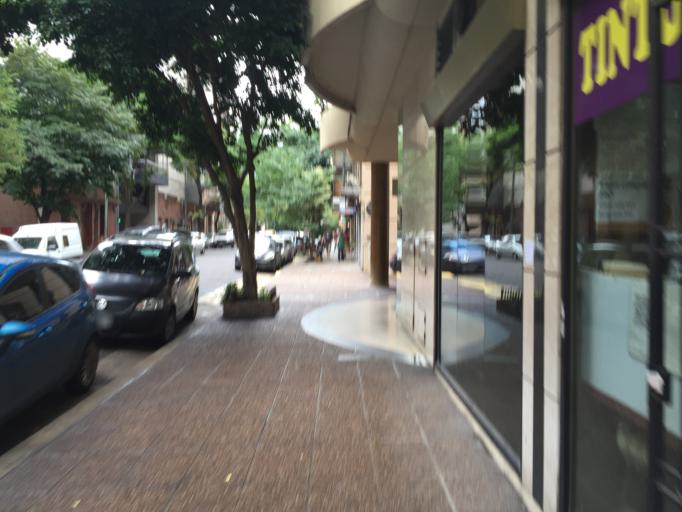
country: AR
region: Buenos Aires F.D.
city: Colegiales
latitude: -34.5736
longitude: -58.4388
